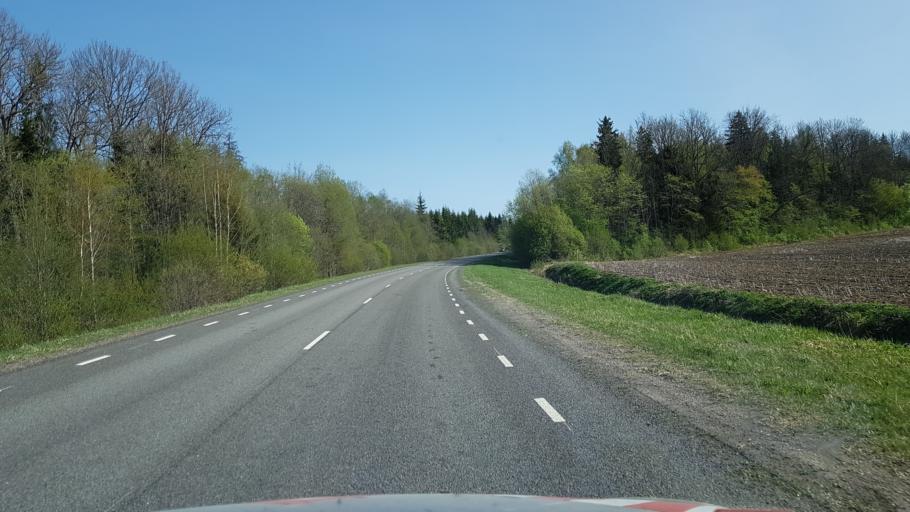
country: EE
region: Viljandimaa
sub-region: Karksi vald
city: Karksi-Nuia
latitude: 58.2071
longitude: 25.5376
